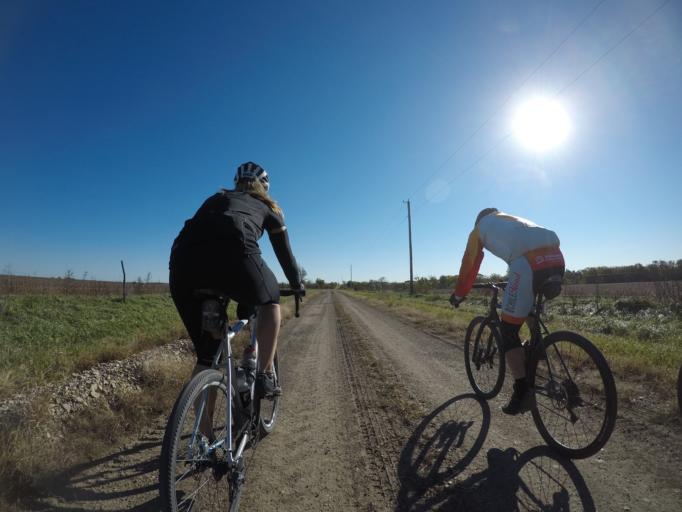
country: US
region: Kansas
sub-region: Morris County
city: Council Grove
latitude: 38.8260
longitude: -96.4117
